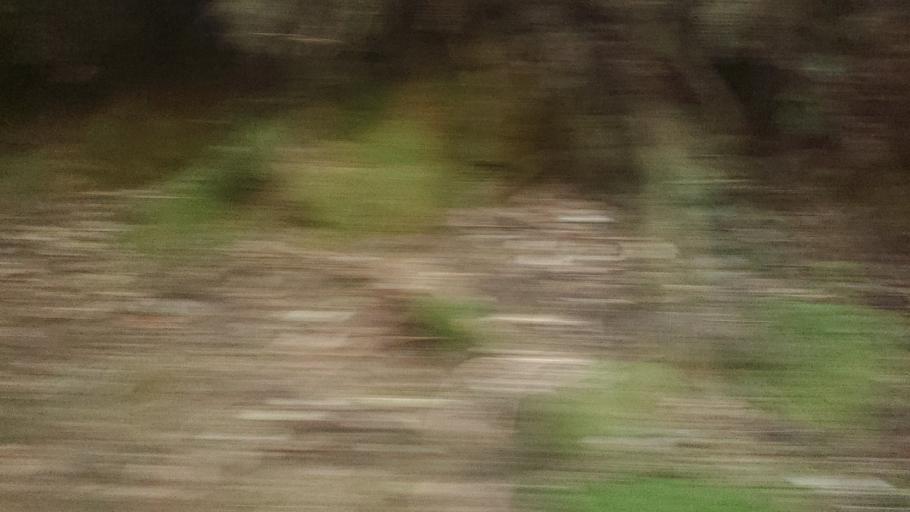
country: TW
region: Taiwan
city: Lugu
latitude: 23.6236
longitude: 120.7191
